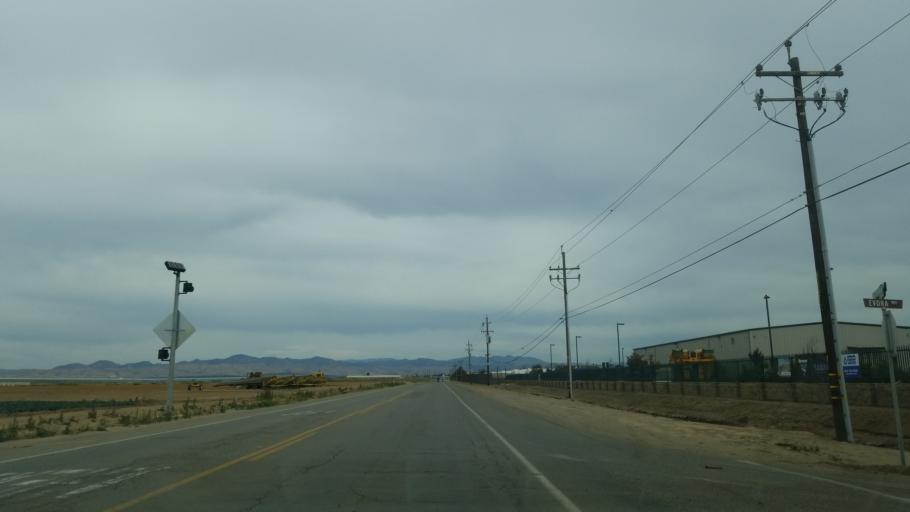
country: US
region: California
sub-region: Santa Barbara County
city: Santa Maria
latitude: 34.9209
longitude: -120.4880
